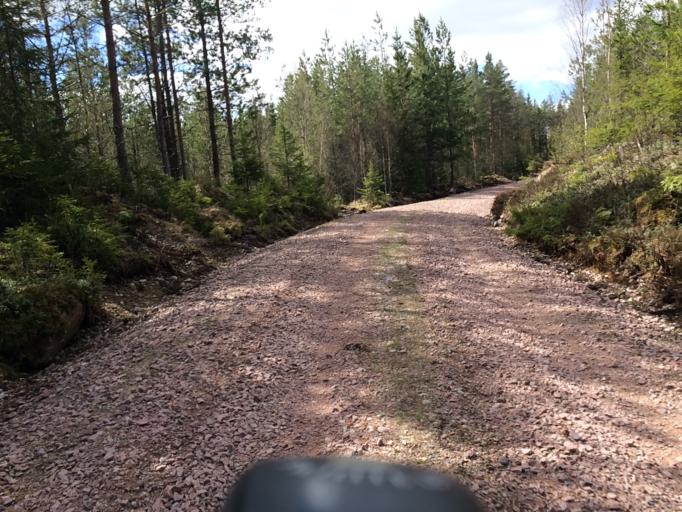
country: SE
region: OErebro
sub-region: Hallefors Kommun
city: Haellefors
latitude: 60.0533
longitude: 14.5204
